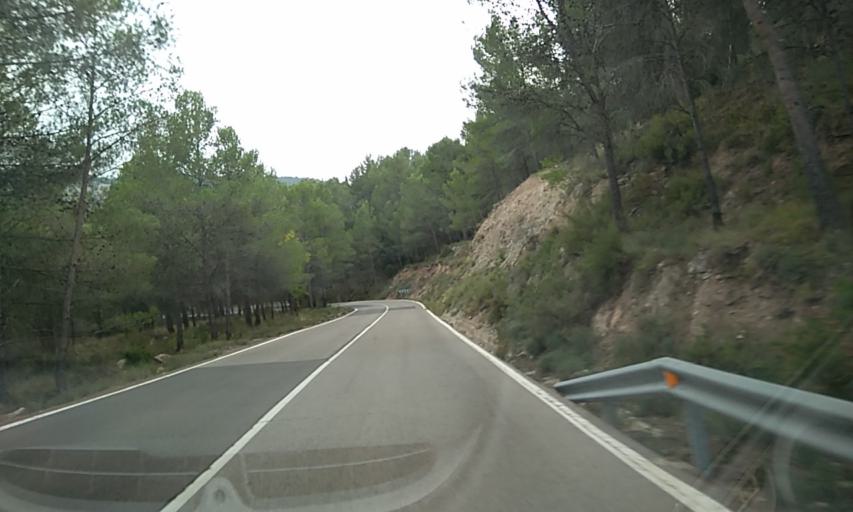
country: ES
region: Valencia
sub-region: Provincia de Castello
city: Puebla de Arenoso
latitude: 40.0930
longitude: -0.5672
